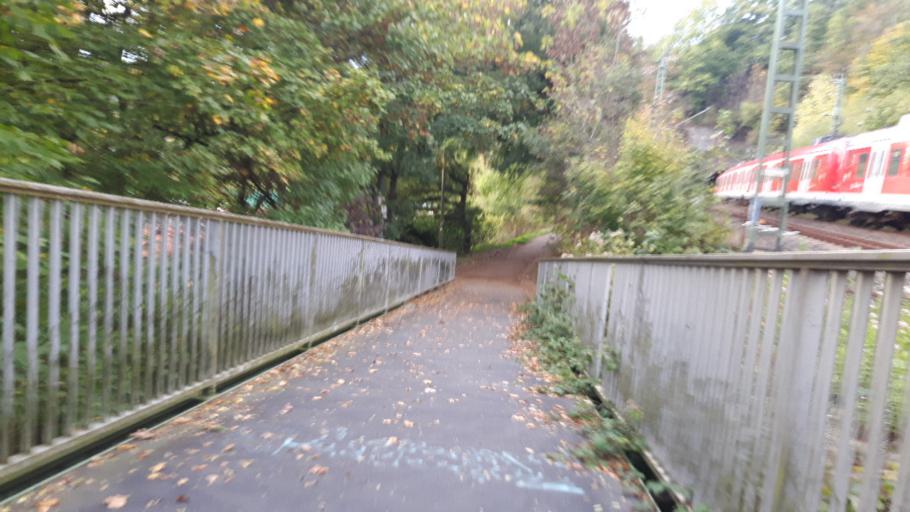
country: DE
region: Rheinland-Pfalz
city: Werkhausen
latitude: 50.7754
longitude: 7.5175
